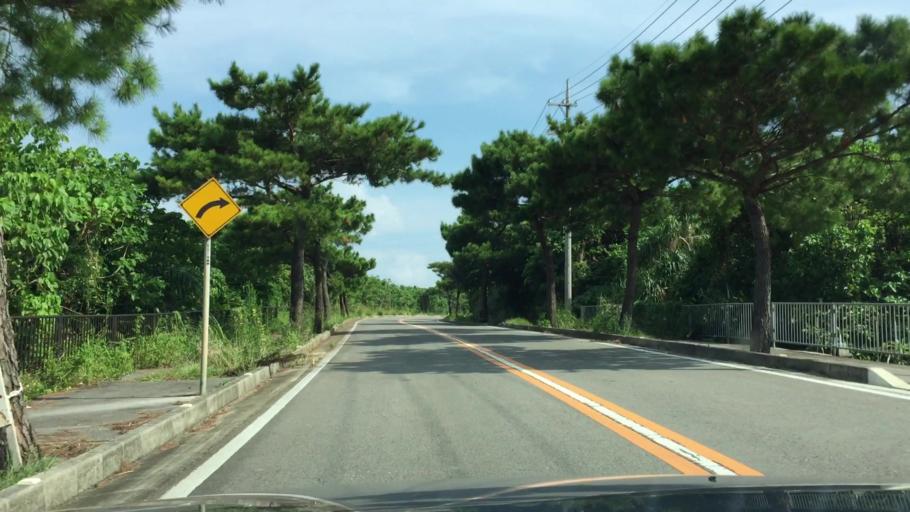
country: JP
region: Okinawa
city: Ishigaki
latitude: 24.4916
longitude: 124.2796
